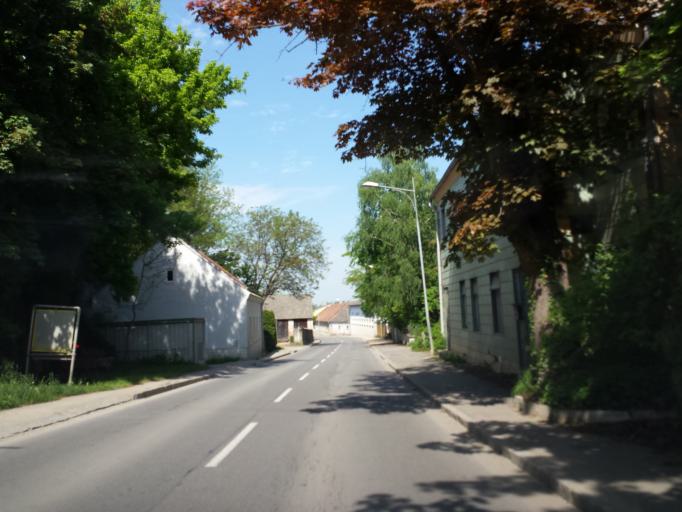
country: AT
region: Lower Austria
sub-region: Politischer Bezirk Tulln
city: Atzenbrugg
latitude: 48.3030
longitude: 15.8968
